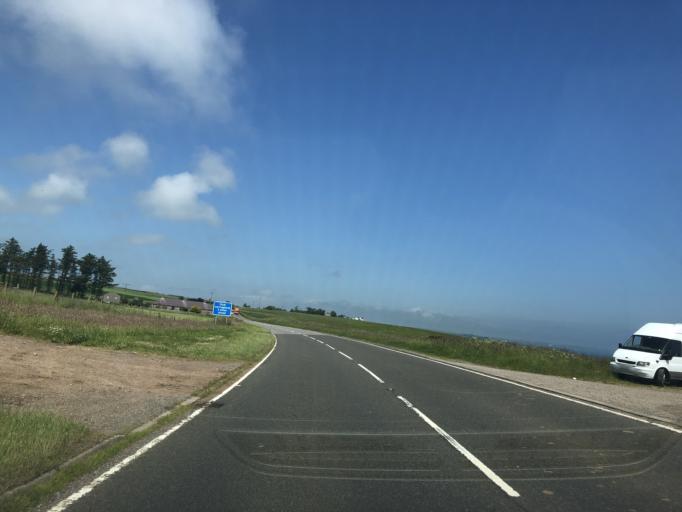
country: GB
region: Scotland
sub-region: Aberdeenshire
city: Stonehaven
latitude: 56.9254
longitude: -2.2048
